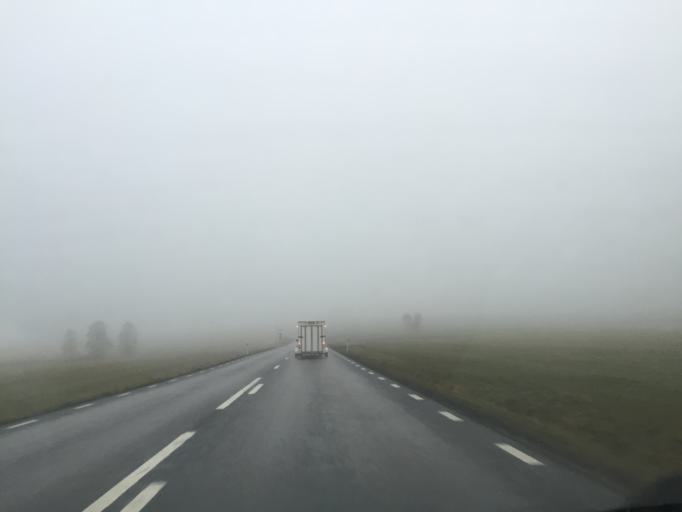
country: SE
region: Soedermanland
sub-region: Katrineholms Kommun
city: Katrineholm
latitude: 58.9486
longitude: 16.3795
